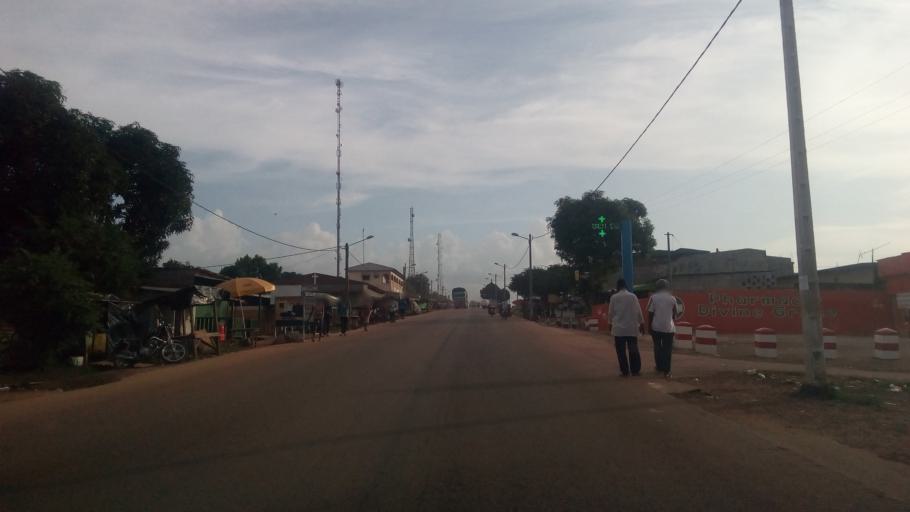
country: CI
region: Dix-Huit Montagnes
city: Duekoue
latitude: 6.7383
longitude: -7.3438
